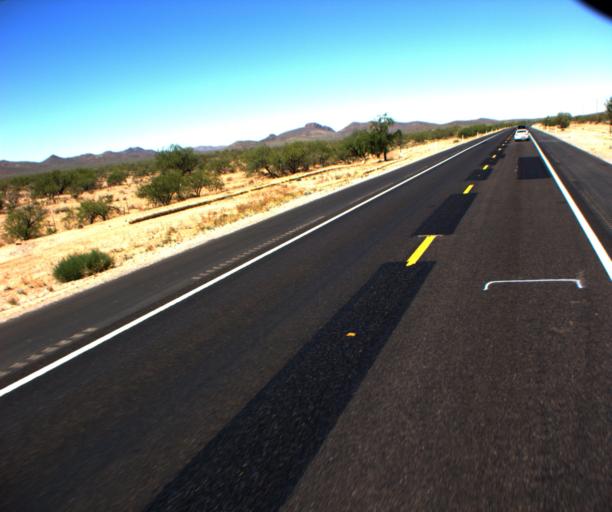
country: US
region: Arizona
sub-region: Pima County
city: Sells
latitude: 31.9212
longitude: -111.8225
